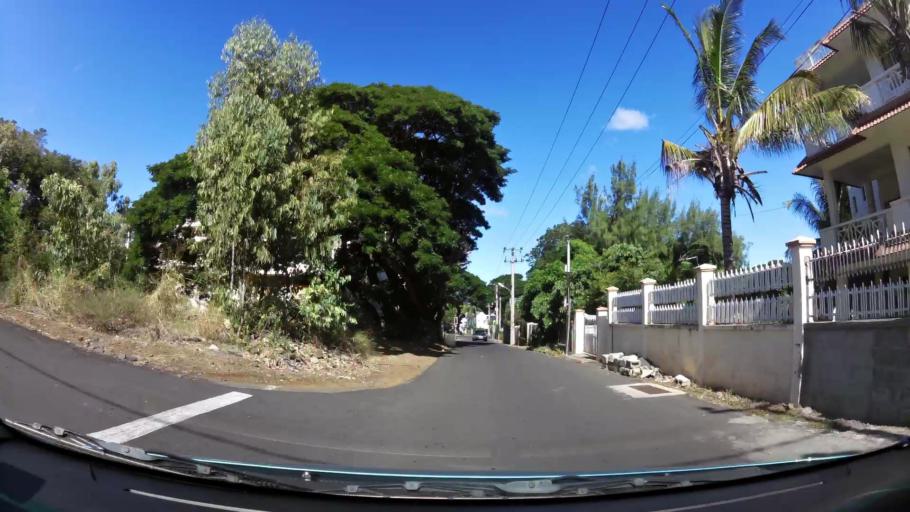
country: MU
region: Black River
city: Flic en Flac
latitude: -20.2754
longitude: 57.3721
